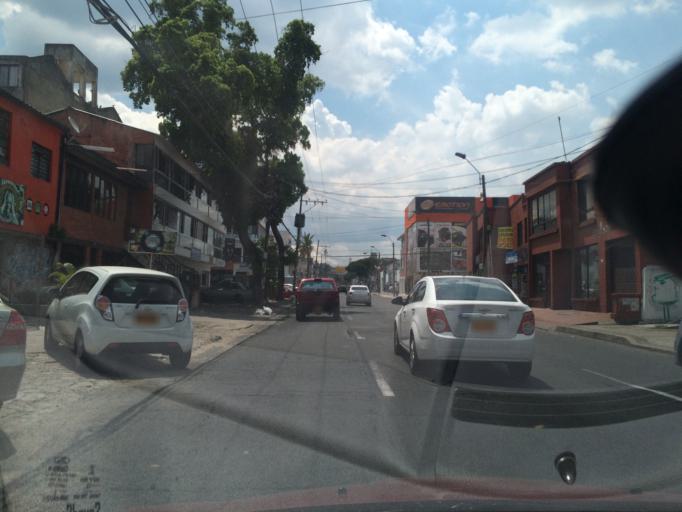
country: CO
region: Valle del Cauca
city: Cali
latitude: 3.4326
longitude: -76.5375
